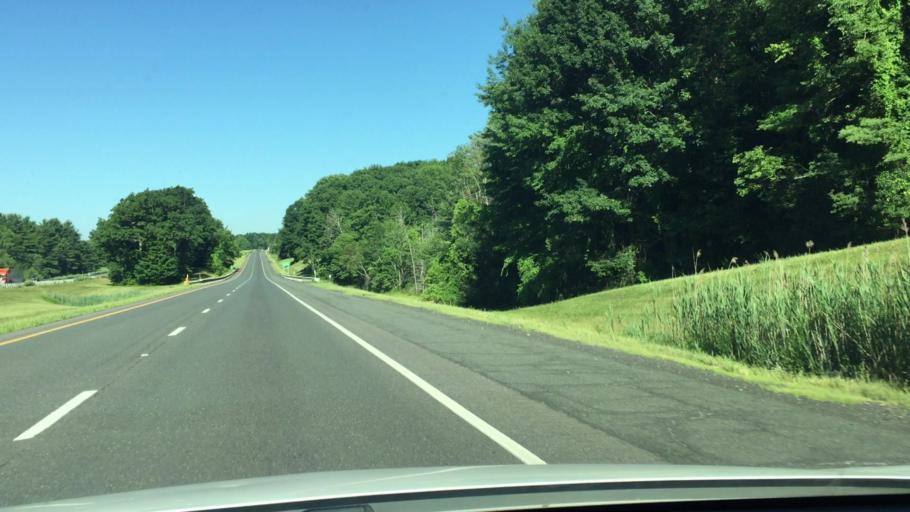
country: US
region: Massachusetts
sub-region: Berkshire County
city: Stockbridge
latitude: 42.2978
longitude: -73.2854
